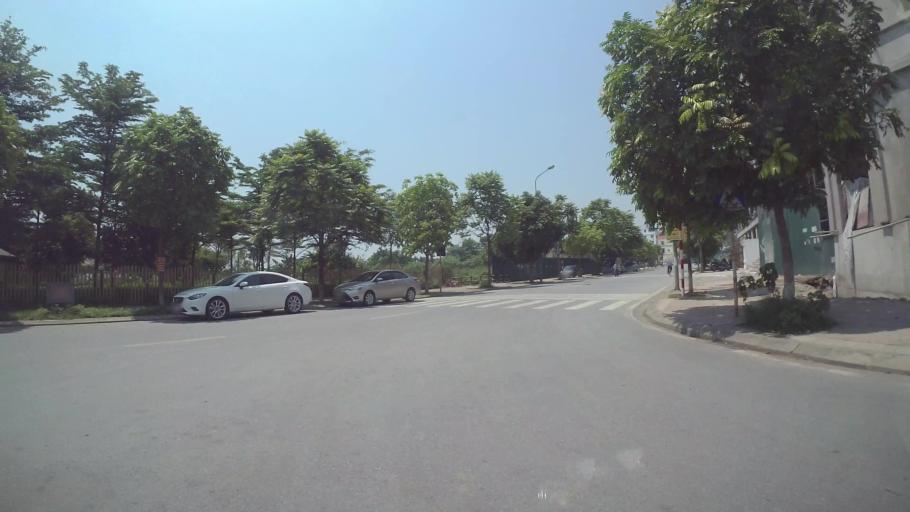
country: VN
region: Ha Noi
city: Hoan Kiem
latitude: 21.0365
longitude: 105.8809
